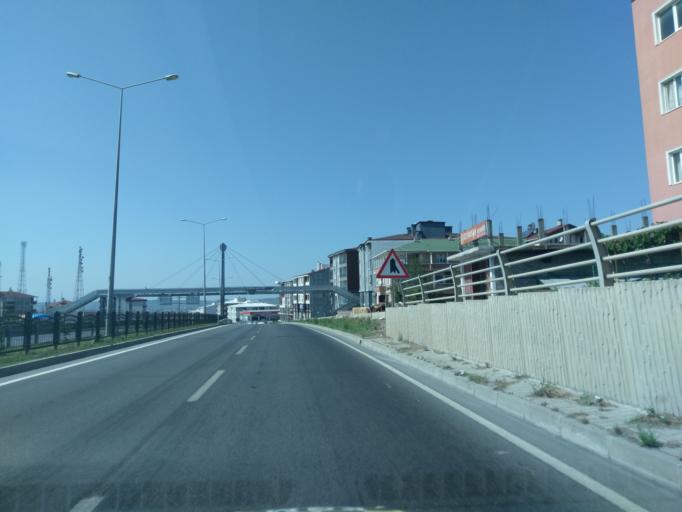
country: TR
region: Samsun
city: Bafra
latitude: 41.5537
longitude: 35.9226
